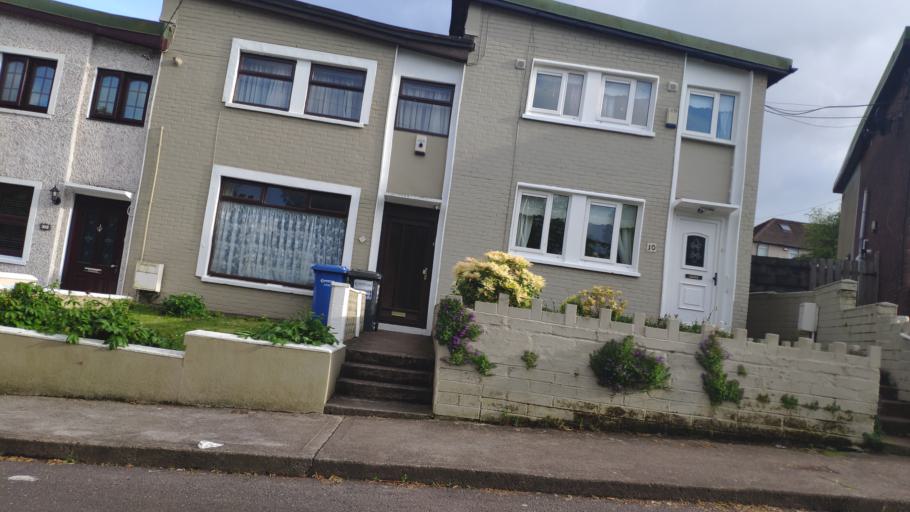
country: IE
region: Munster
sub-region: County Cork
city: Cork
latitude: 51.9060
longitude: -8.4888
